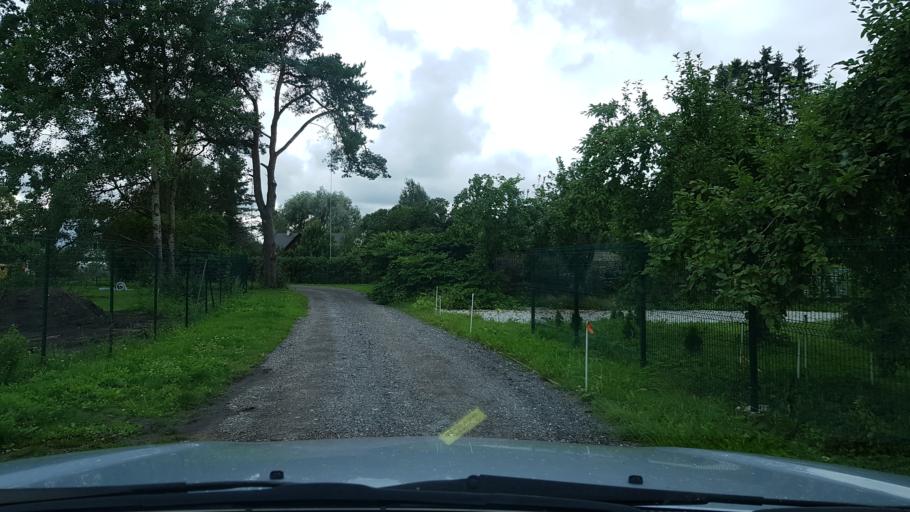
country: EE
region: Harju
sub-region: Joelaehtme vald
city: Loo
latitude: 59.3895
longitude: 24.9642
